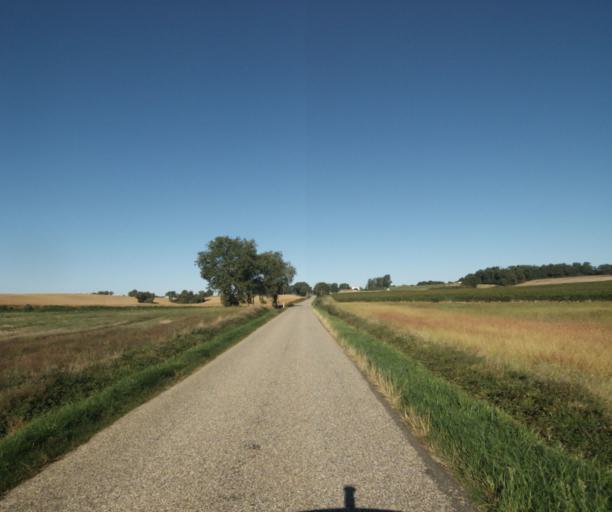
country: FR
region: Midi-Pyrenees
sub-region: Departement du Gers
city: Gondrin
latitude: 43.8274
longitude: 0.2652
